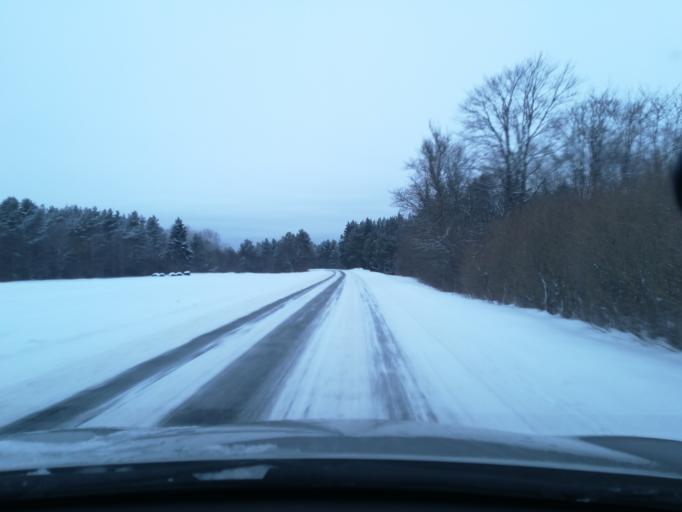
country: EE
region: Harju
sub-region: Keila linn
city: Keila
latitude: 59.3614
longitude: 24.3379
